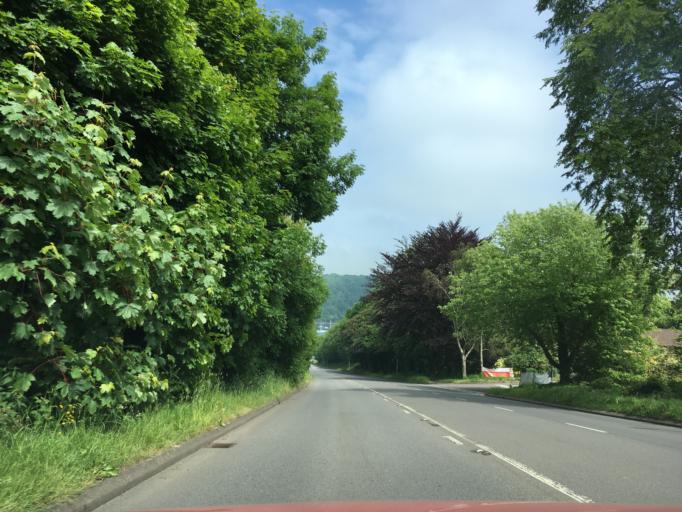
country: GB
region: England
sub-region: Devon
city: Dartmouth
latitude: 50.3537
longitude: -3.5846
